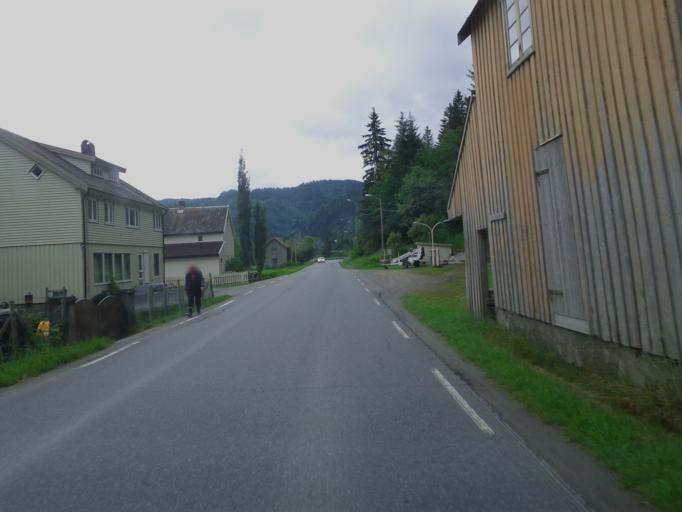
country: NO
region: Sor-Trondelag
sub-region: Midtre Gauldal
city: Storen
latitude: 63.0076
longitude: 10.4518
